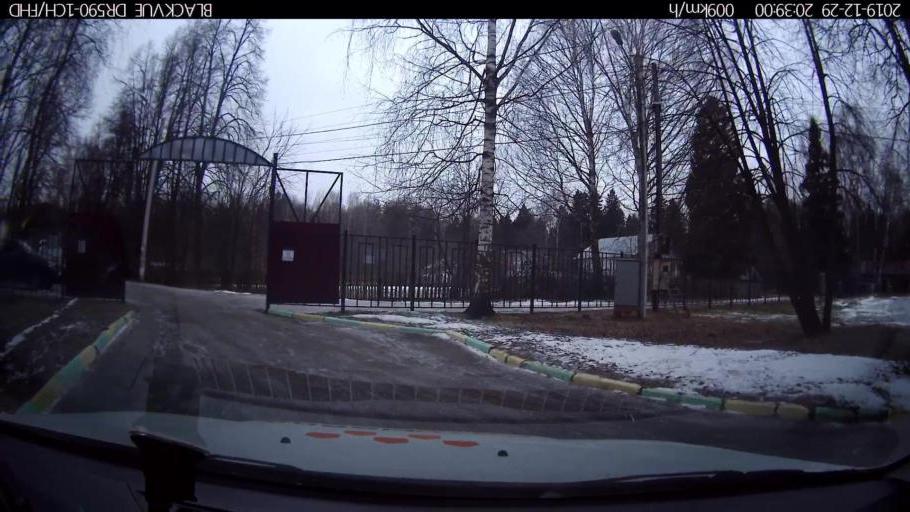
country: RU
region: Nizjnij Novgorod
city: Afonino
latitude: 56.1933
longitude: 44.0488
